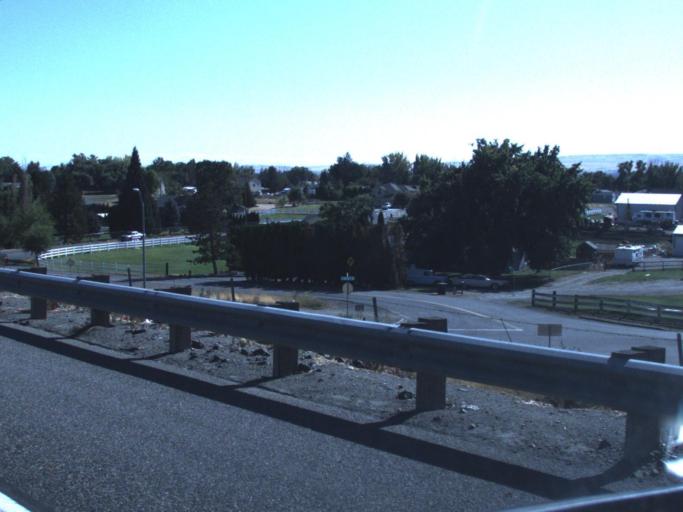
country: US
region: Washington
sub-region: Franklin County
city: West Pasco
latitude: 46.2569
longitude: -119.1547
